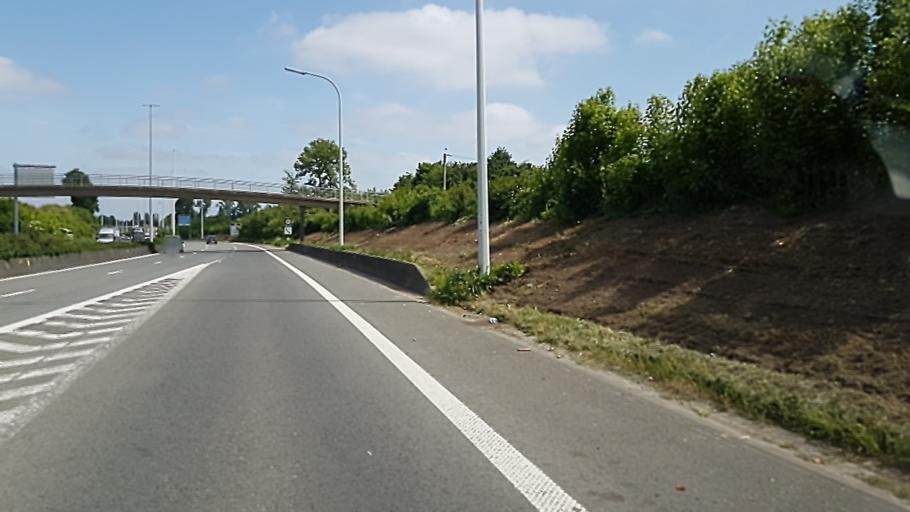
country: BE
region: Flanders
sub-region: Provincie West-Vlaanderen
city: Kortrijk
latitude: 50.8376
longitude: 3.2225
